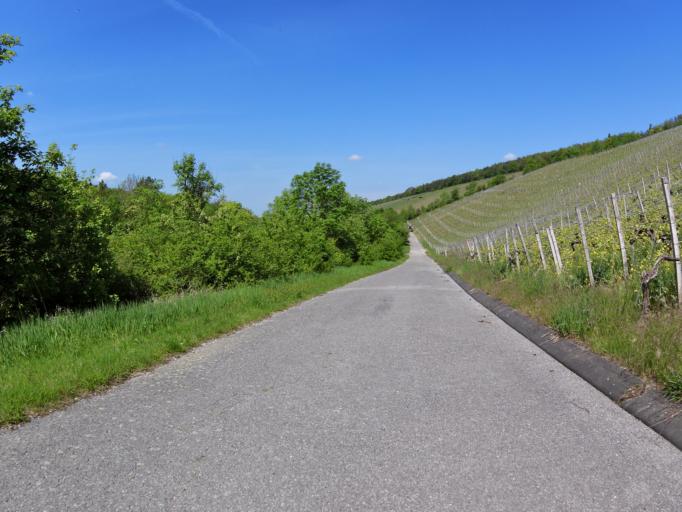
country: DE
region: Bavaria
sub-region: Regierungsbezirk Unterfranken
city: Eibelstadt
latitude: 49.7336
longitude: 10.0144
